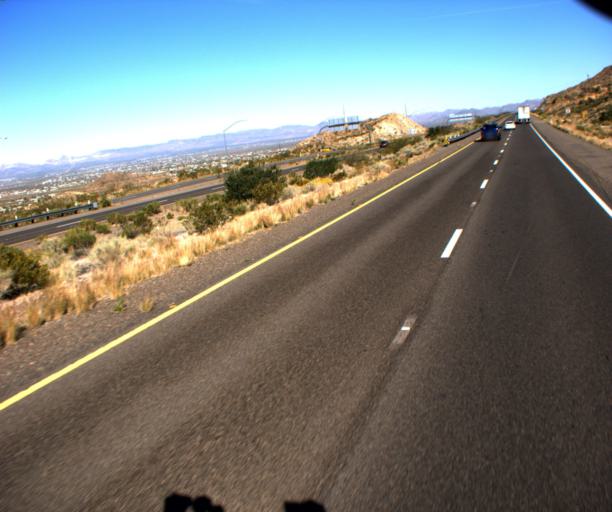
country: US
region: Arizona
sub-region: Mohave County
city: Kingman
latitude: 35.2234
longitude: -114.1282
